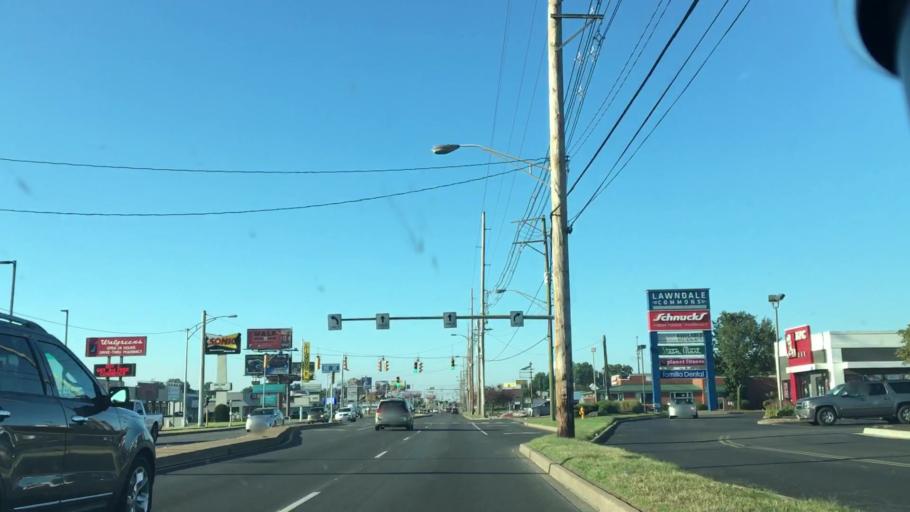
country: US
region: Indiana
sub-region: Vanderburgh County
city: Evansville
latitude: 37.9633
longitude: -87.4926
